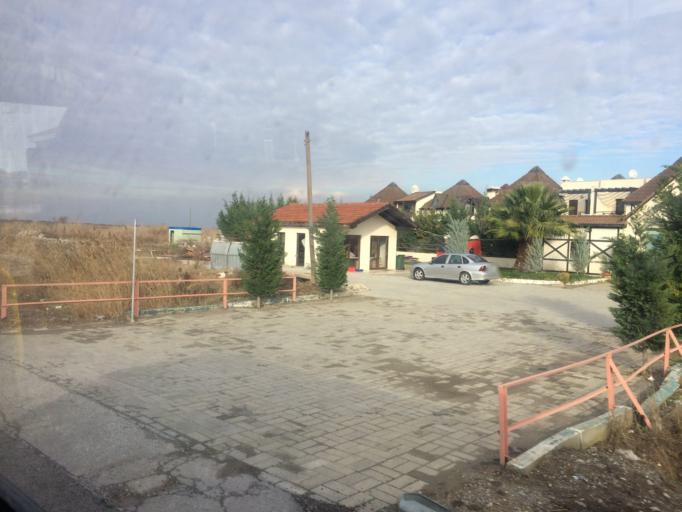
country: TR
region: Izmir
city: Menemen
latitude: 38.5067
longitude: 26.9584
